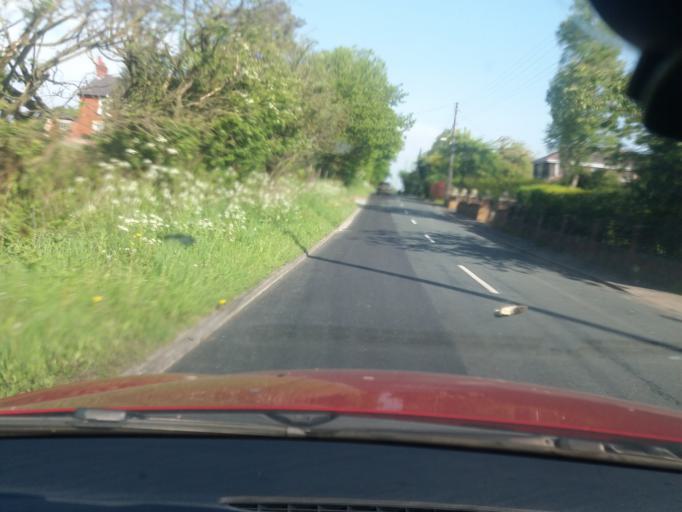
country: GB
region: England
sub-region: Lancashire
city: Adlington
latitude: 53.6298
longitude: -2.5909
